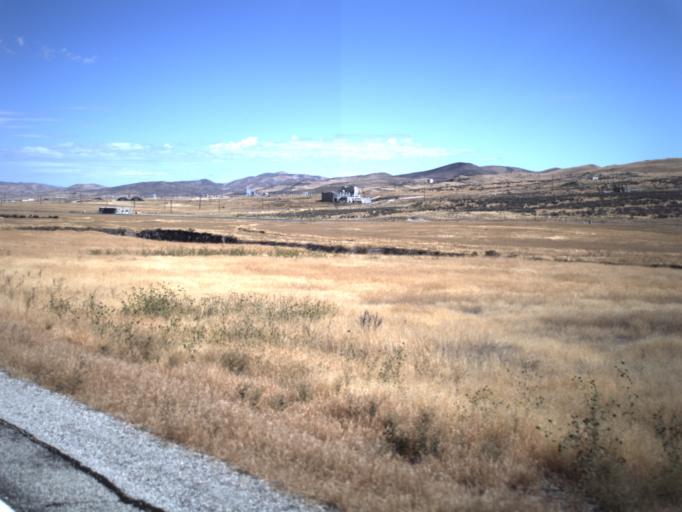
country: US
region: Utah
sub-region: Box Elder County
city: Tremonton
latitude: 41.6863
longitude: -112.4441
